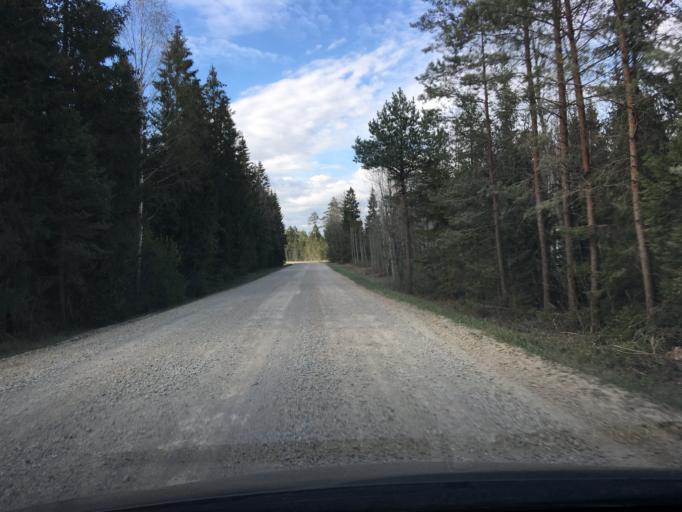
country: EE
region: Raplamaa
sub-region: Maerjamaa vald
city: Marjamaa
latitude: 58.9634
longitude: 24.3308
